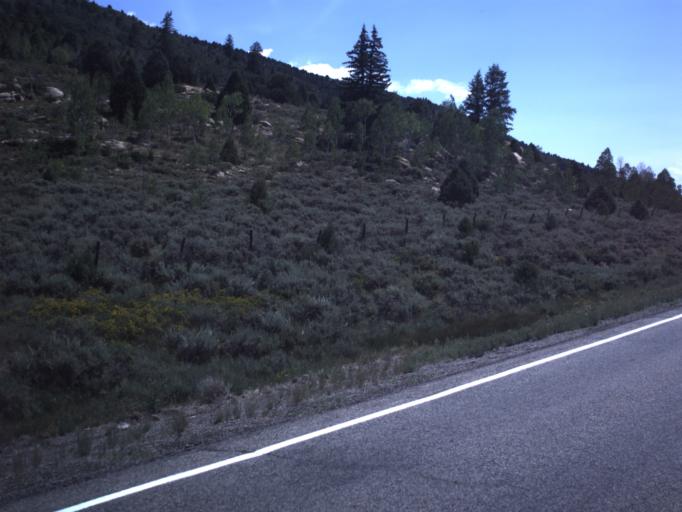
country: US
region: Utah
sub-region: Carbon County
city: Helper
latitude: 39.8593
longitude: -111.1063
